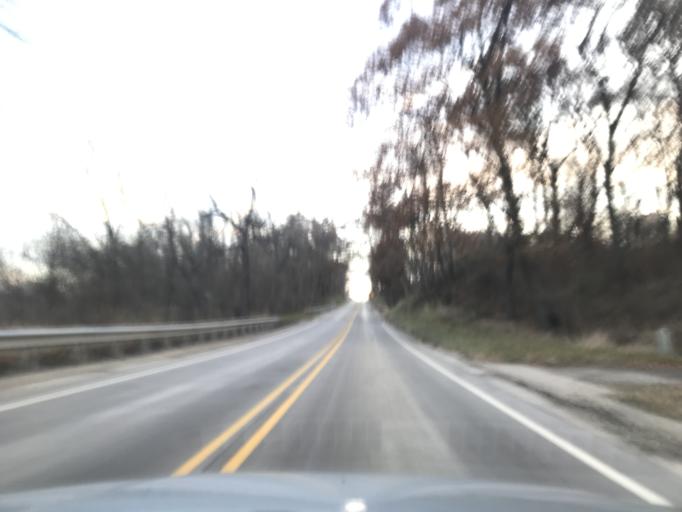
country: US
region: Illinois
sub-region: Henderson County
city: Oquawka
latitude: 40.9025
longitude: -90.8645
